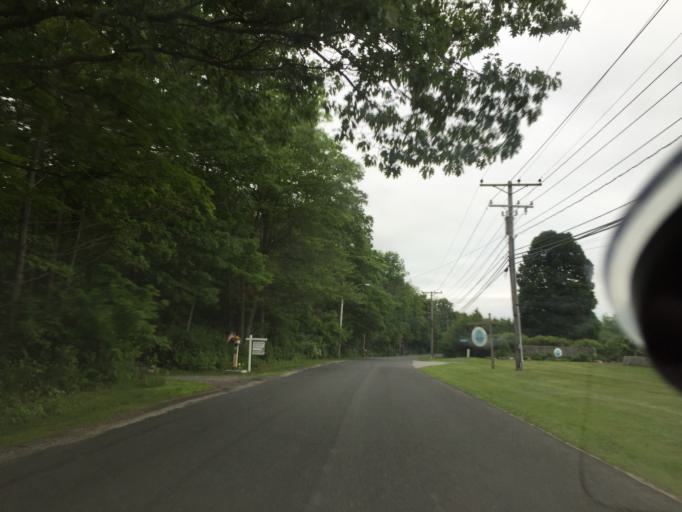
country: US
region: Connecticut
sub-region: Litchfield County
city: Litchfield
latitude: 41.8248
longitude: -73.2498
